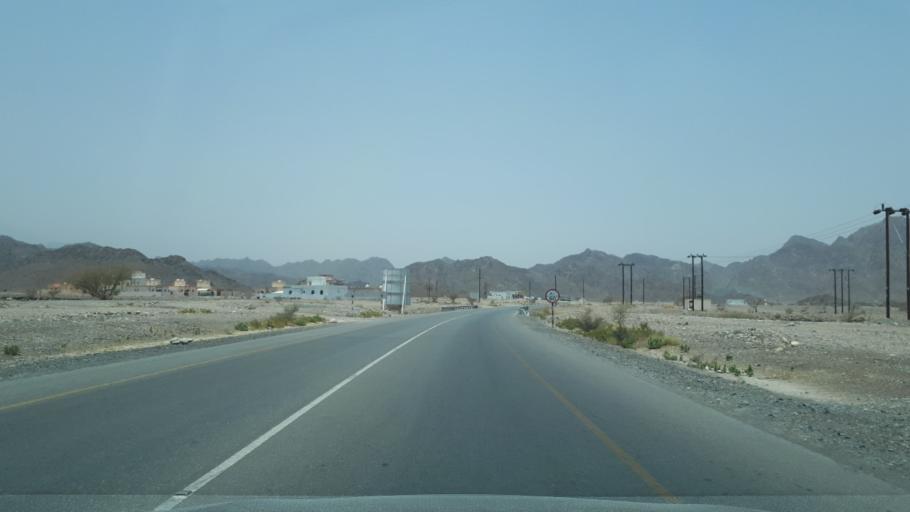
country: OM
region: Al Batinah
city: Rustaq
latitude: 23.4104
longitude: 57.3464
